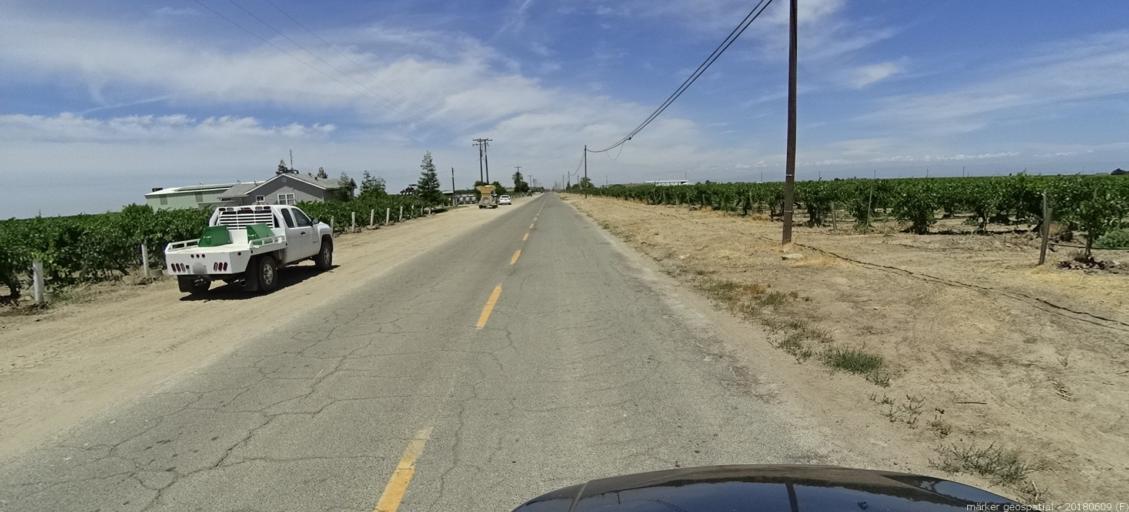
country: US
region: California
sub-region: Fresno County
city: Biola
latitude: 36.8468
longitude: -120.0921
